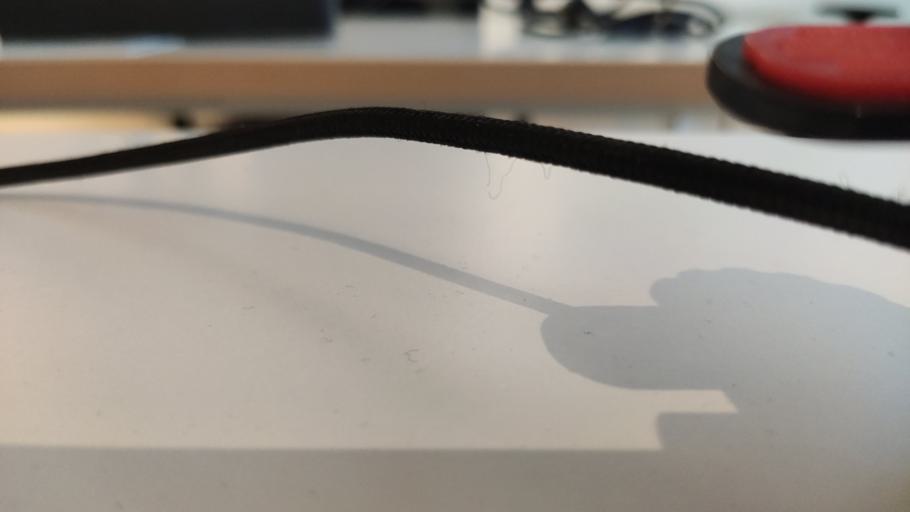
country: RU
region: Moskovskaya
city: Novopetrovskoye
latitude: 55.9181
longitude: 36.4388
